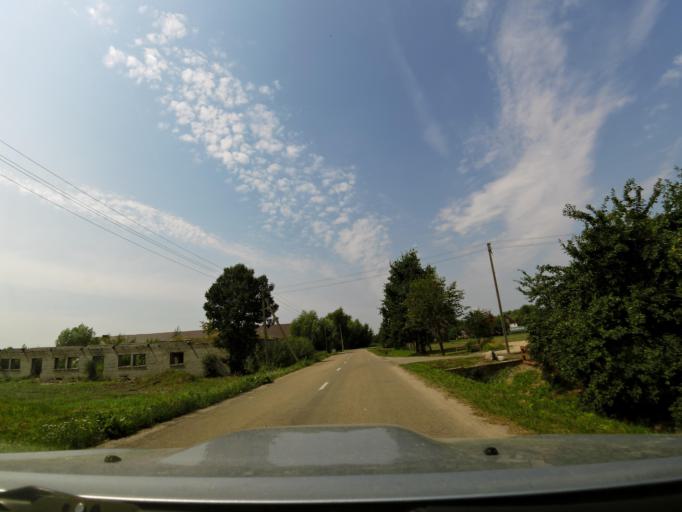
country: LT
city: Rusne
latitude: 55.3432
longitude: 21.3194
